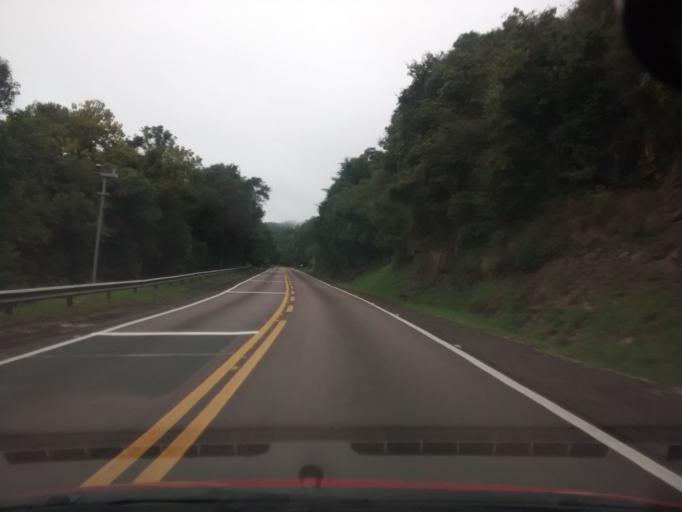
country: BR
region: Rio Grande do Sul
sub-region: Vacaria
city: Estrela
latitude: -28.1982
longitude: -50.7556
